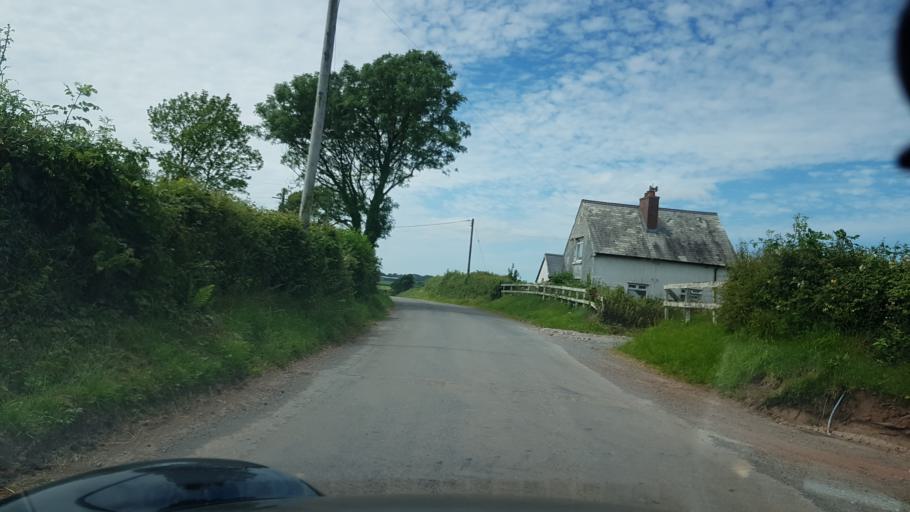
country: GB
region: Wales
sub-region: Carmarthenshire
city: Llanddowror
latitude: 51.7683
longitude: -4.5132
